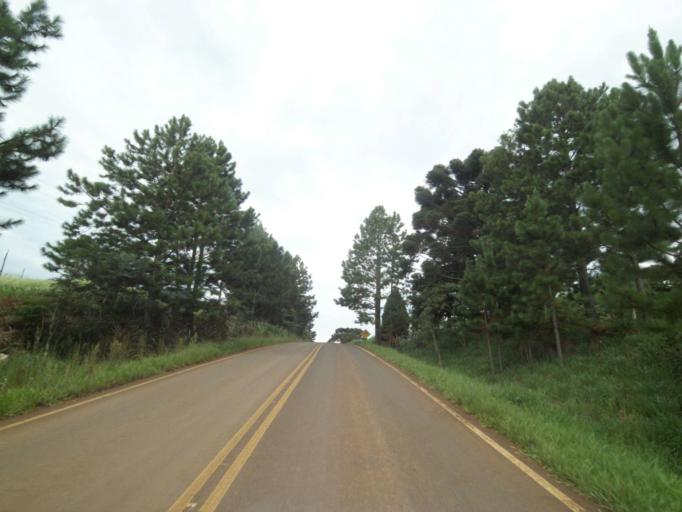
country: BR
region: Parana
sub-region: Pitanga
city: Pitanga
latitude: -24.8950
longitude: -51.9623
